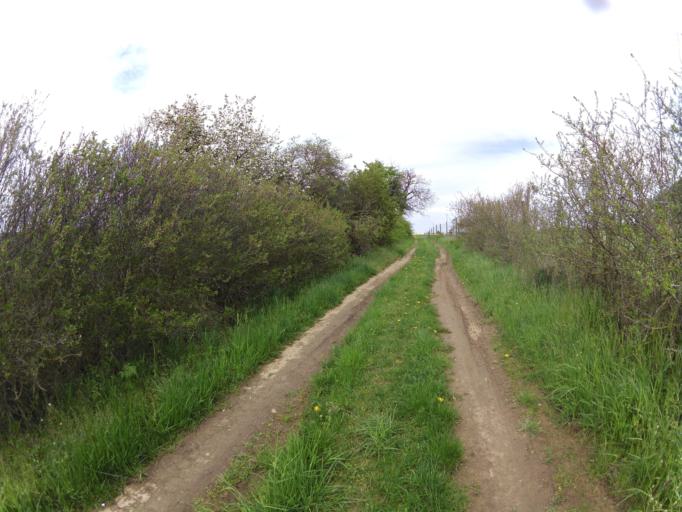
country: DE
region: Bavaria
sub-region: Regierungsbezirk Unterfranken
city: Prosselsheim
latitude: 49.8608
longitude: 10.1456
